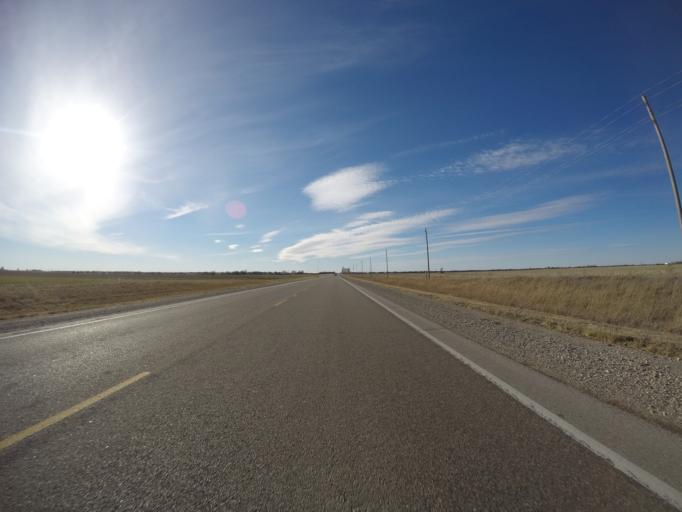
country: US
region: Kansas
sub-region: McPherson County
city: Moundridge
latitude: 38.3769
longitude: -97.4375
